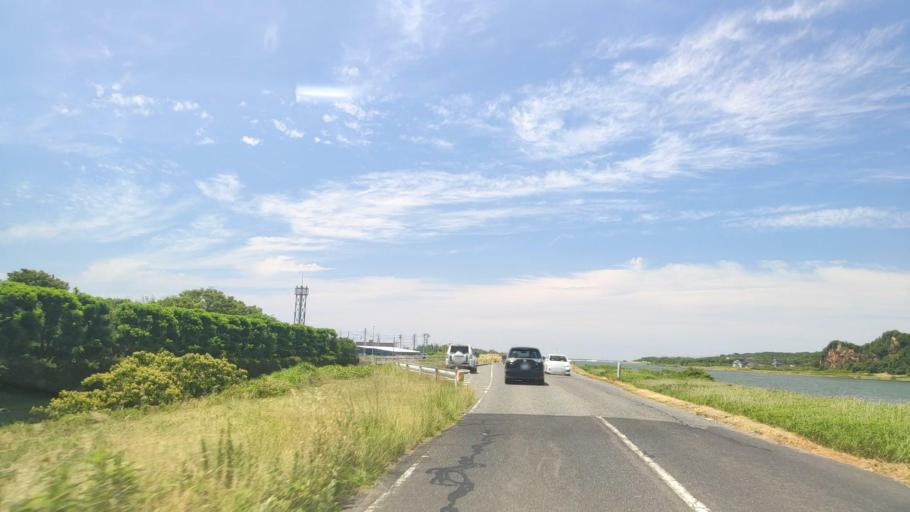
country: JP
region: Tottori
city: Tottori
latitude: 35.5243
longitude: 134.2054
